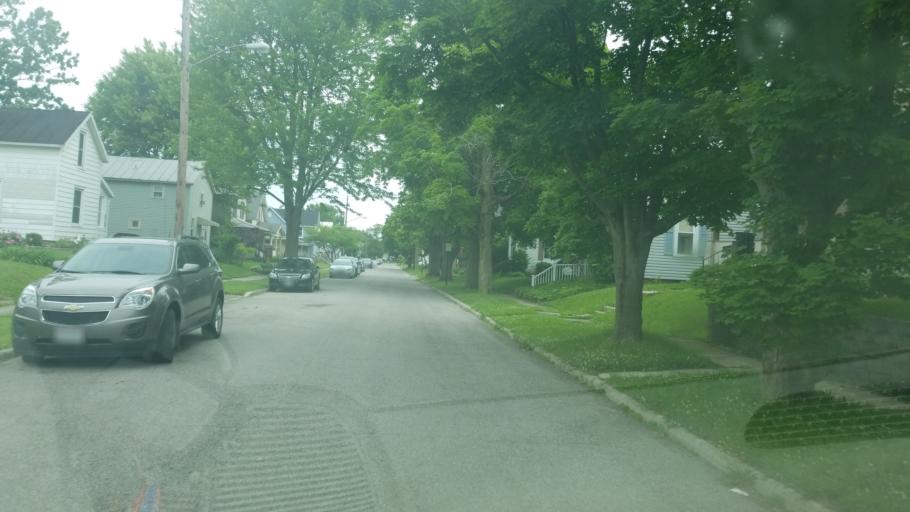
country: US
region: Ohio
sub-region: Crawford County
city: Bucyrus
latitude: 40.7981
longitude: -82.9696
